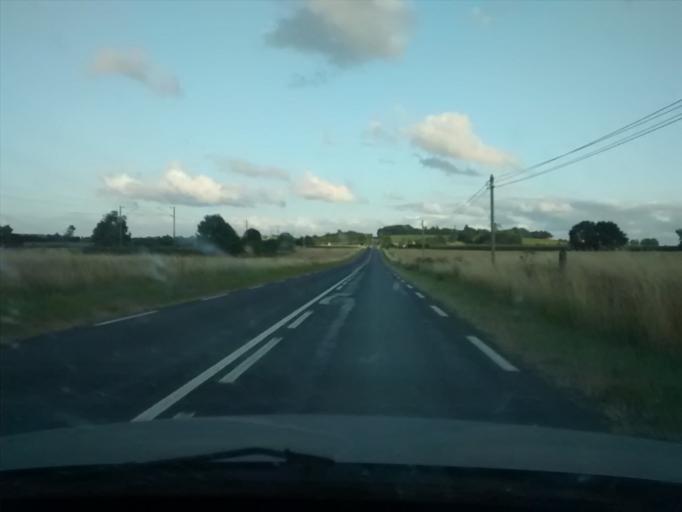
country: FR
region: Pays de la Loire
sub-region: Departement de la Sarthe
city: Conlie
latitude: 48.1415
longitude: -0.0485
